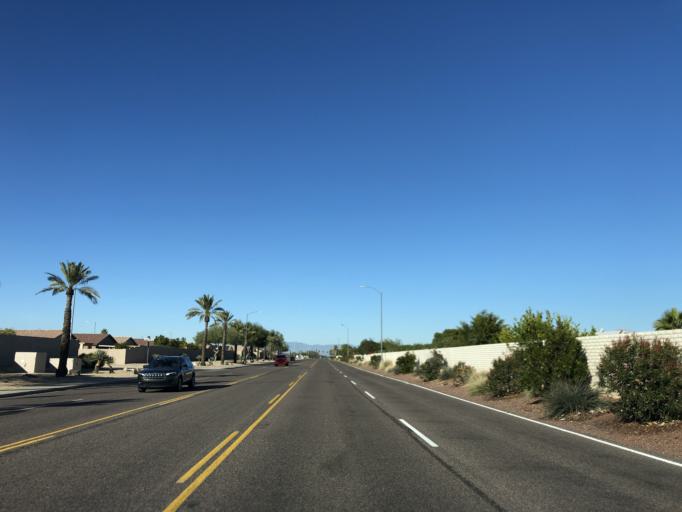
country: US
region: Arizona
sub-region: Maricopa County
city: Sun City West
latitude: 33.6628
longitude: -112.2899
